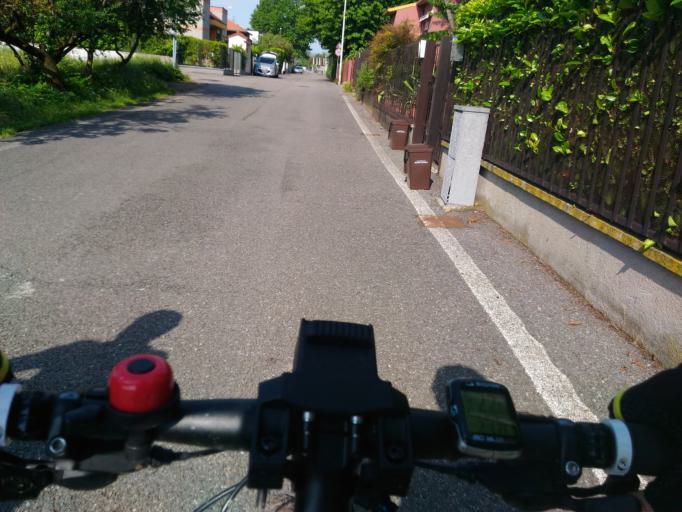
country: IT
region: Lombardy
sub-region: Provincia di Lodi
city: Montanaso Lombardo
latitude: 45.3223
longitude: 9.4653
